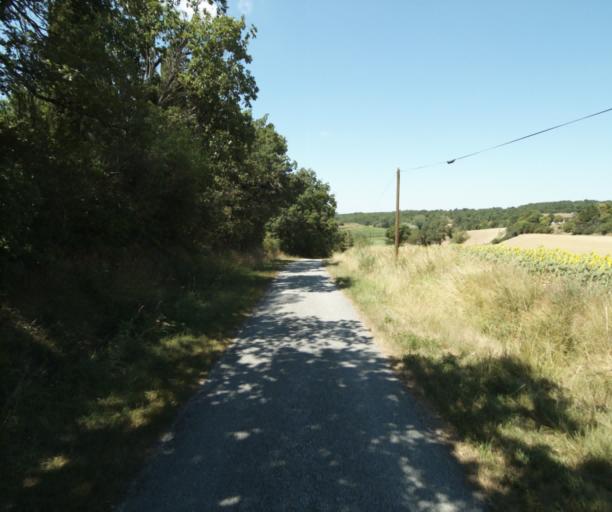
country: FR
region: Midi-Pyrenees
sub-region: Departement de la Haute-Garonne
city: Saint-Felix-Lauragais
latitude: 43.4800
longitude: 1.8579
